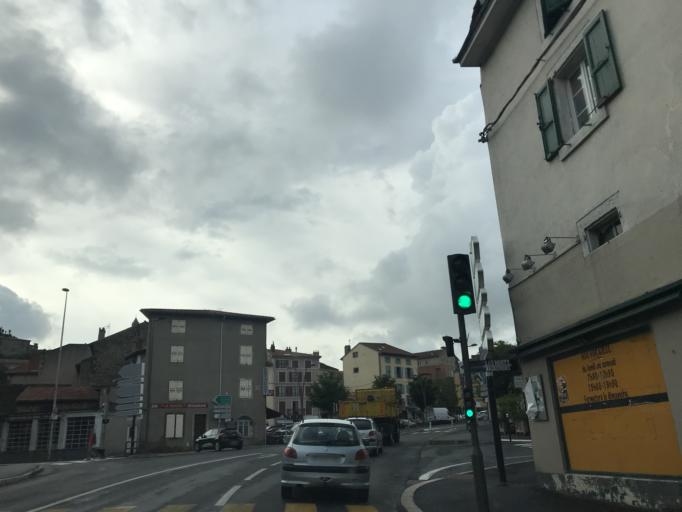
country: FR
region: Auvergne
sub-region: Departement de la Haute-Loire
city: Le Puy-en-Velay
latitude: 45.0472
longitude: 3.8789
